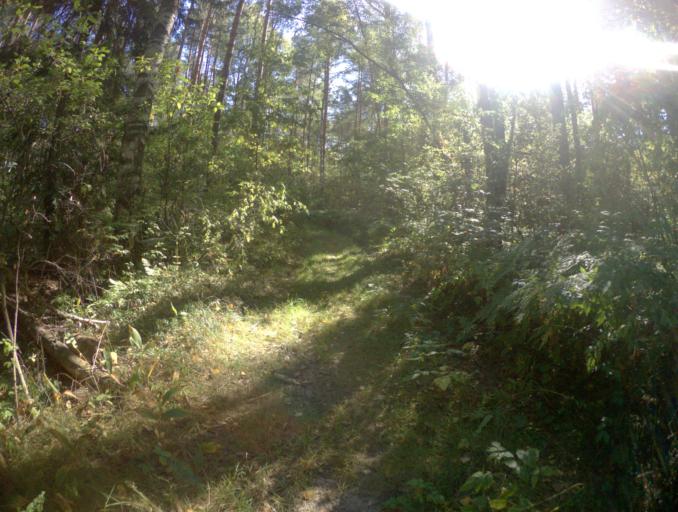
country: RU
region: Vladimir
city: Krasnaya Gorbatka
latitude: 55.7894
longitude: 41.6590
